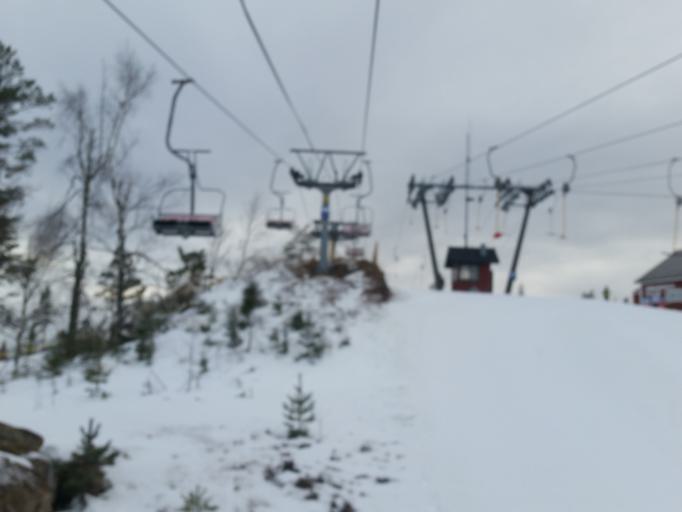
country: SE
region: Gaevleborg
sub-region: Sandvikens Kommun
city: Jarbo
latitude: 60.7510
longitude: 16.4909
